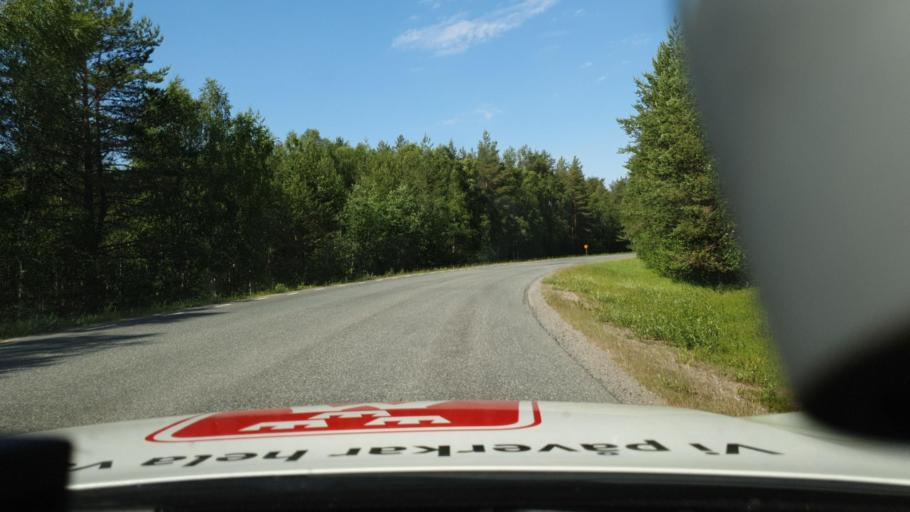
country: SE
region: Norrbotten
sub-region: Kalix Kommun
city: Rolfs
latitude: 65.8676
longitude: 23.1193
